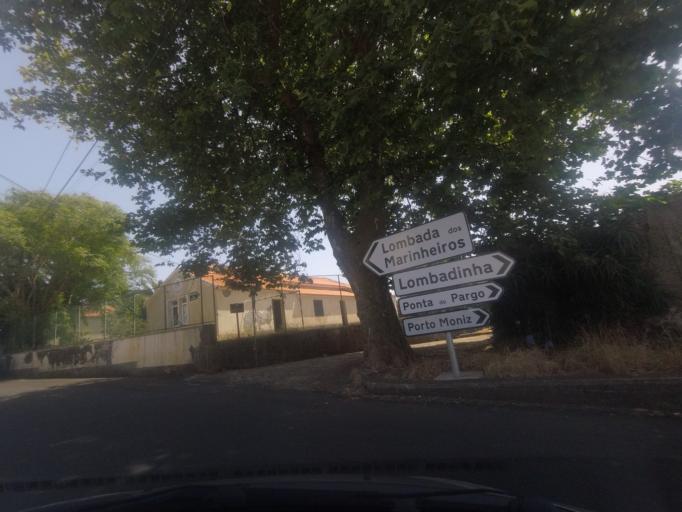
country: PT
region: Madeira
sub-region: Calheta
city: Faja da Ovelha
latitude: 32.8016
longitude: -17.2408
